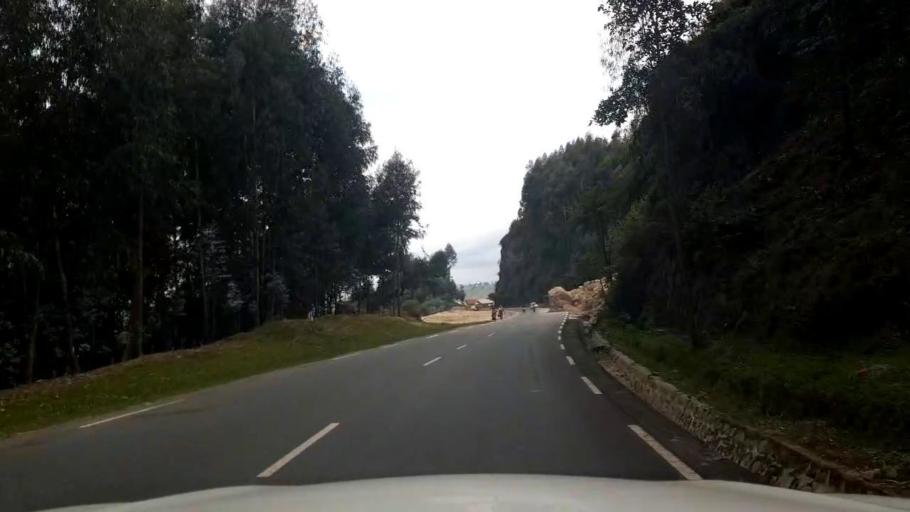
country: RW
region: Northern Province
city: Musanze
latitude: -1.6699
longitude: 29.5145
